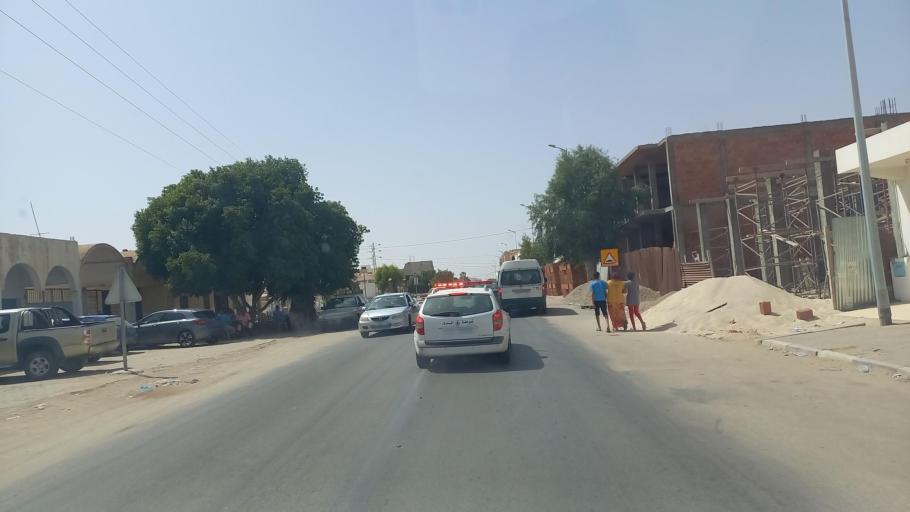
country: TN
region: Madanin
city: Medenine
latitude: 33.3271
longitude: 10.4846
